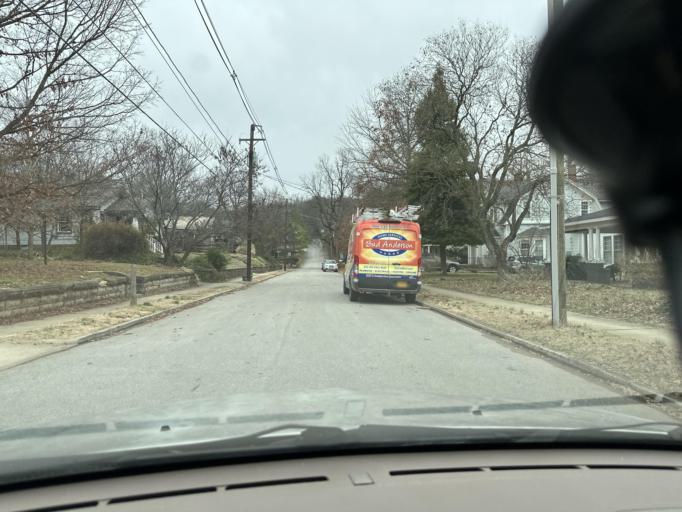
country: US
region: Arkansas
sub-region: Washington County
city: Fayetteville
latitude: 36.0674
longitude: -94.1542
